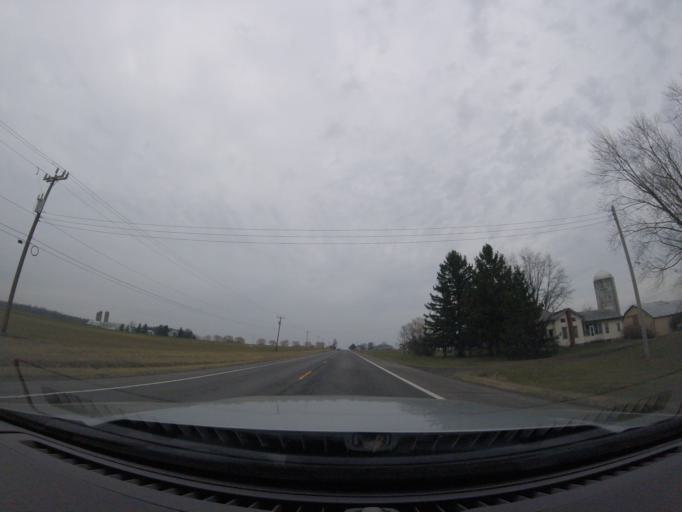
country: US
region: New York
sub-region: Yates County
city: Dundee
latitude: 42.6232
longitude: -76.9436
